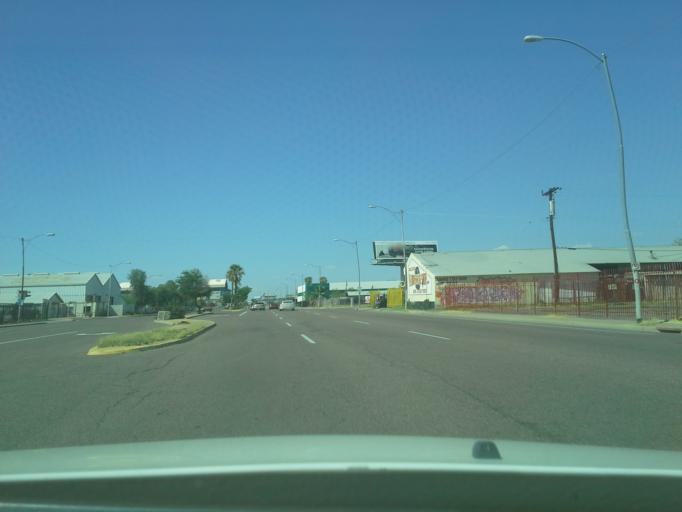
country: US
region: Arizona
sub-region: Maricopa County
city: Phoenix
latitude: 33.4322
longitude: -112.0651
